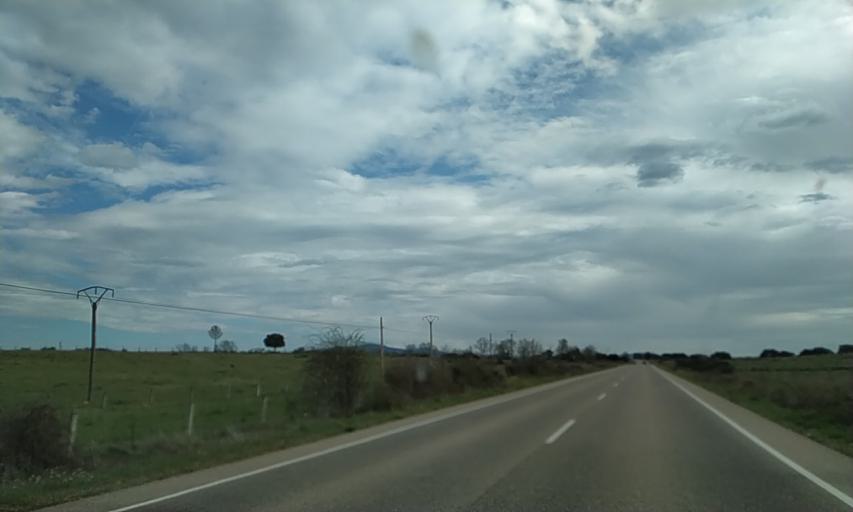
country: ES
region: Castille and Leon
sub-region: Provincia de Salamanca
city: Robleda
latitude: 40.4020
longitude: -6.6054
